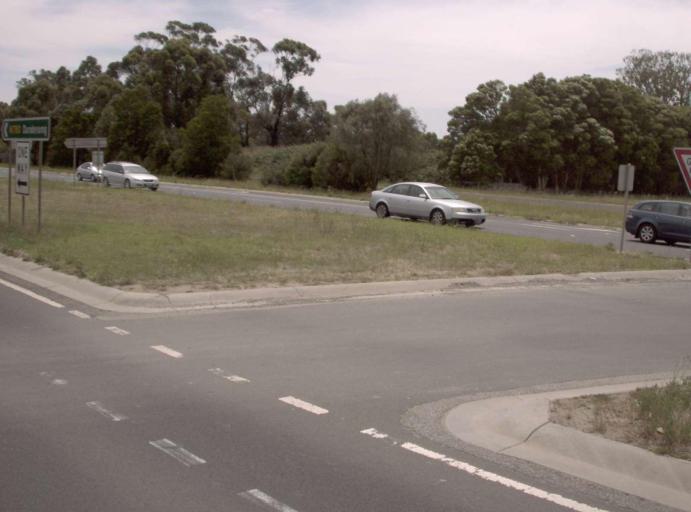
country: AU
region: Victoria
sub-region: Casey
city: Lynbrook
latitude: -38.0543
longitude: 145.2438
